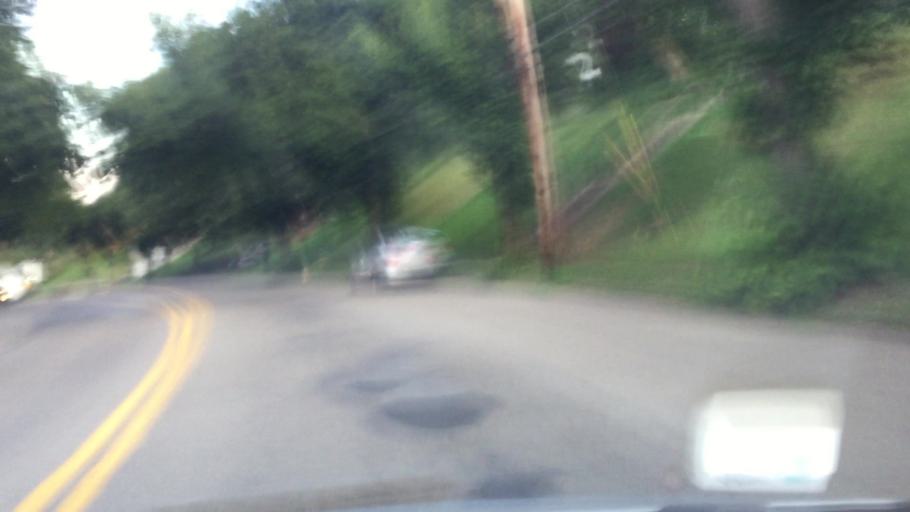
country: US
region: Pennsylvania
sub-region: Allegheny County
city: Homestead
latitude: 40.4233
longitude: -79.9199
